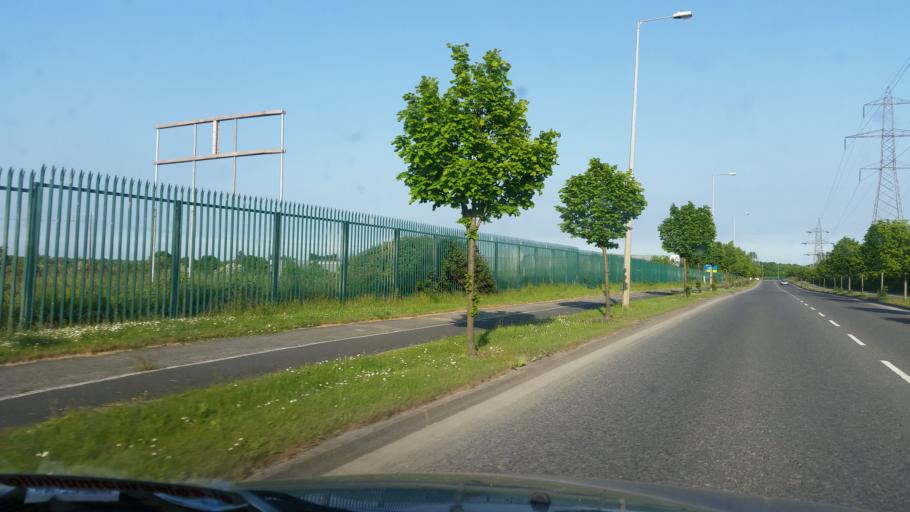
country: IE
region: Leinster
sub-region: Fingal County
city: Blanchardstown
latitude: 53.4150
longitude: -6.3529
